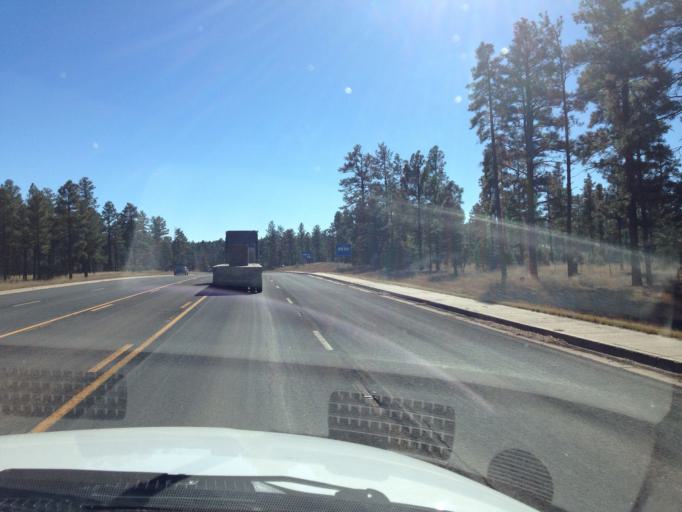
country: US
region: Arizona
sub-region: Navajo County
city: Show Low
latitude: 34.2477
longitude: -110.0720
